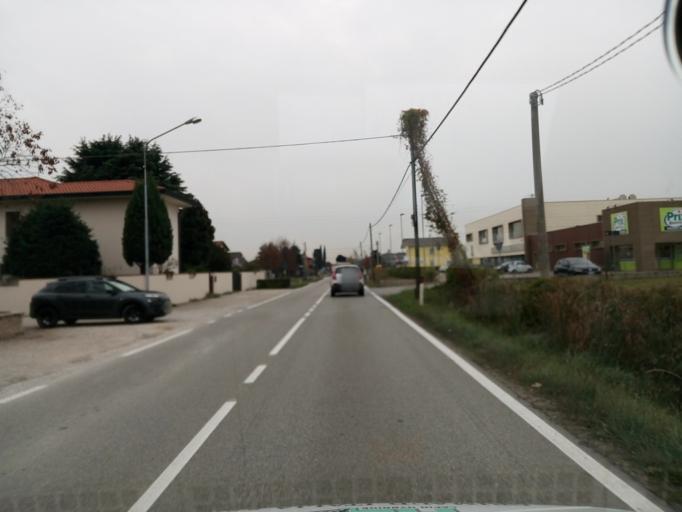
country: IT
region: Veneto
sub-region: Provincia di Padova
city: Villanova
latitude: 45.4896
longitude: 11.9681
